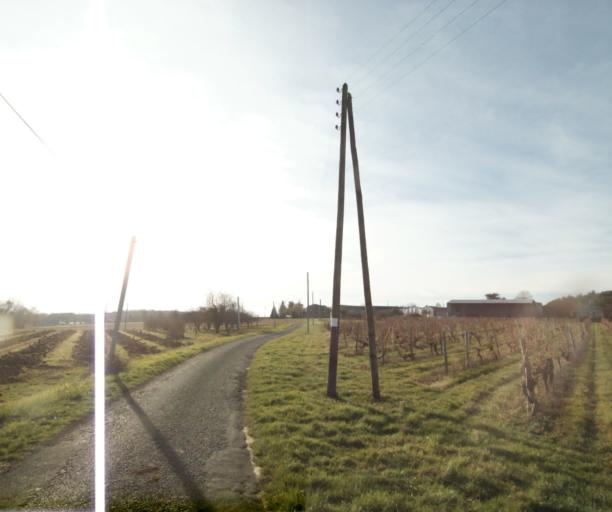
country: FR
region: Poitou-Charentes
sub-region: Departement de la Charente-Maritime
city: Chaniers
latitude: 45.7326
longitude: -0.5168
